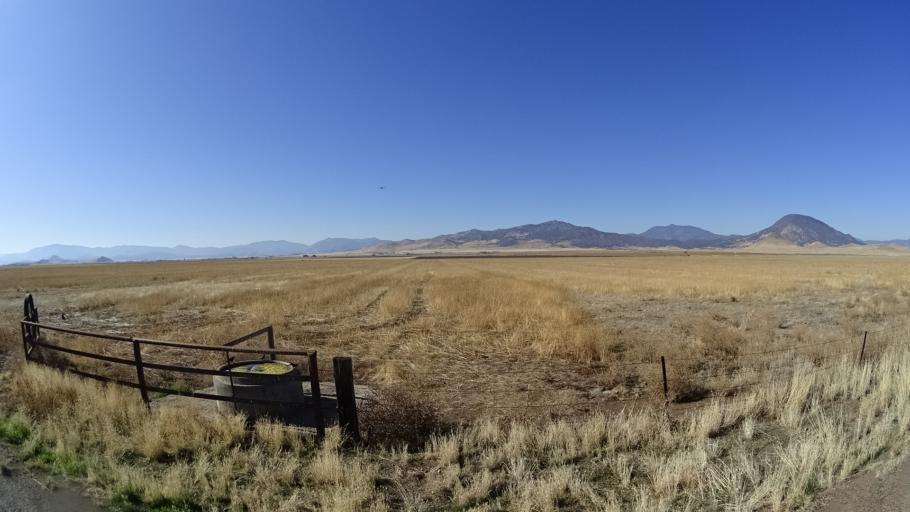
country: US
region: California
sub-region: Siskiyou County
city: Montague
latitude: 41.7906
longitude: -122.4343
